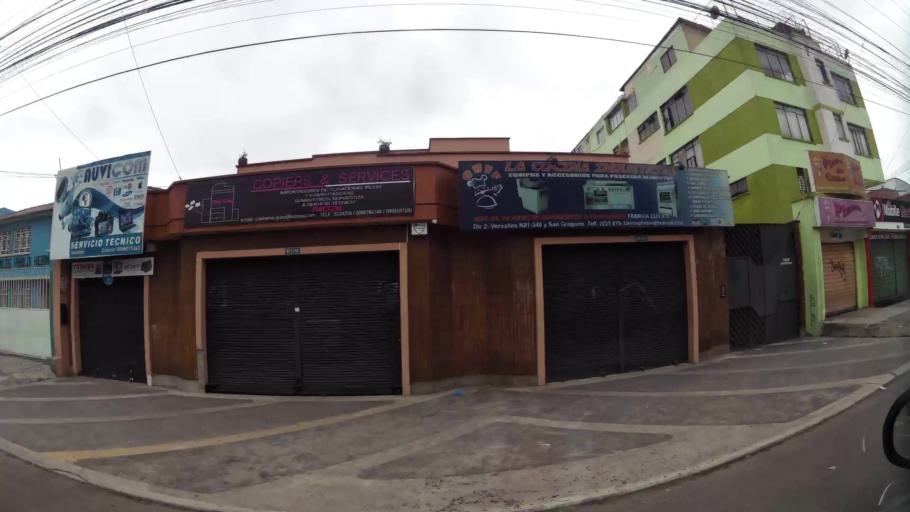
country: EC
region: Pichincha
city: Quito
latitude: -0.2023
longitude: -78.4999
